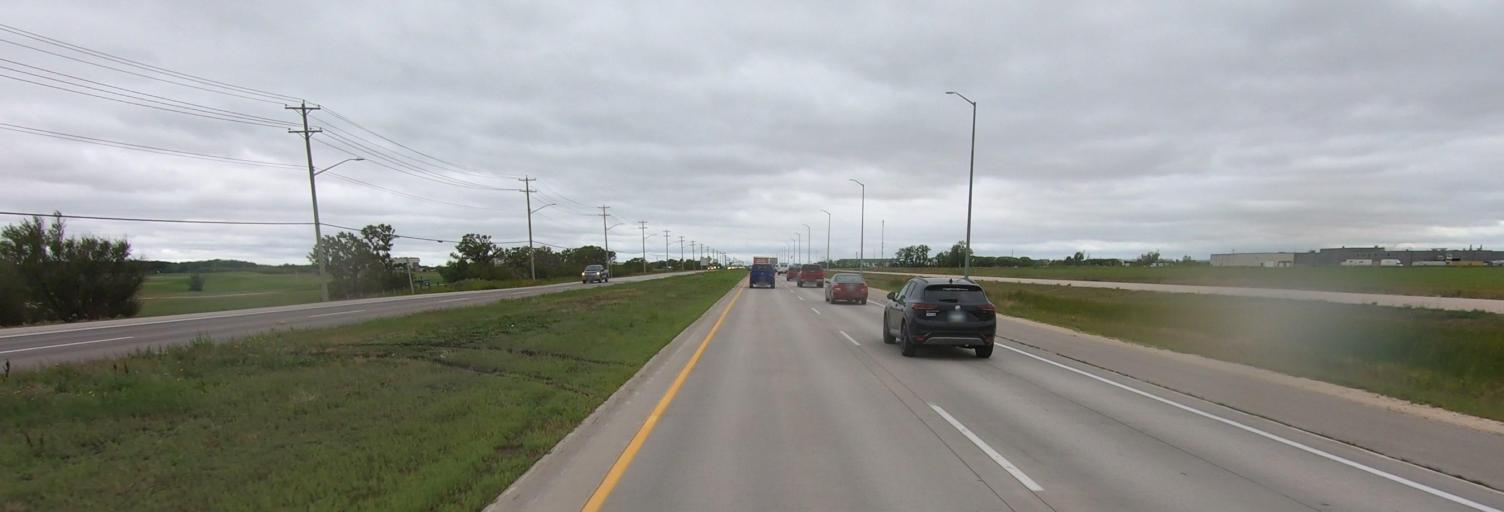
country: CA
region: Manitoba
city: Headingley
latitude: 49.8762
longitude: -97.3647
